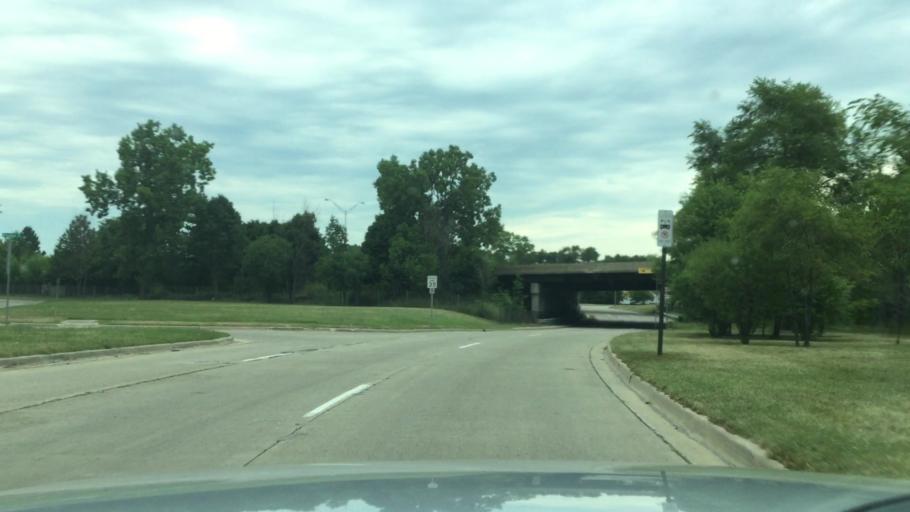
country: US
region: Michigan
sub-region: Genesee County
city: Beecher
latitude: 43.0639
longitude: -83.6824
